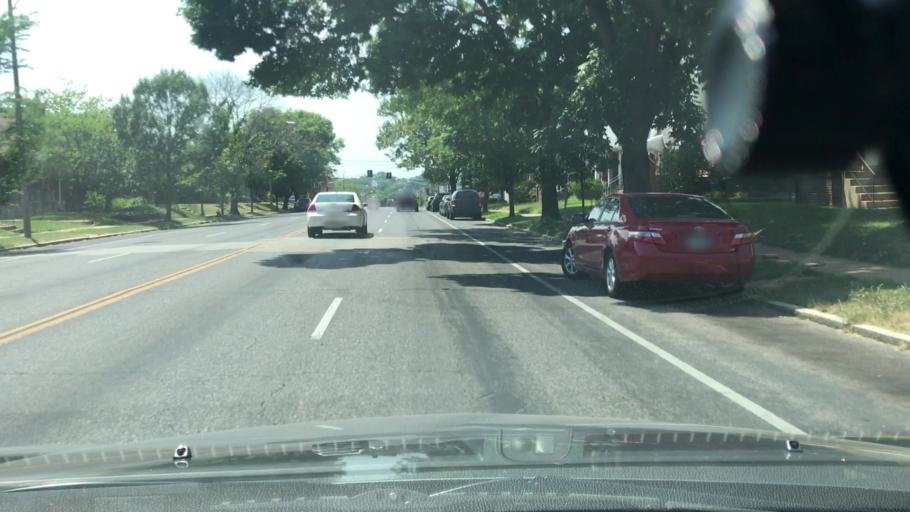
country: US
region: Missouri
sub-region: Saint Louis County
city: Maplewood
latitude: 38.5930
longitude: -90.2898
